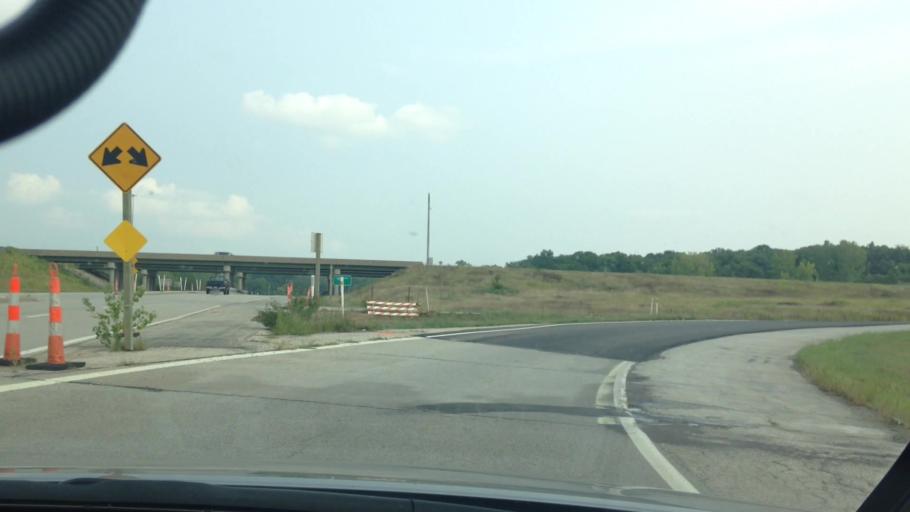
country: US
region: Missouri
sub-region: Platte County
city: Weatherby Lake
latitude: 39.1808
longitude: -94.8008
